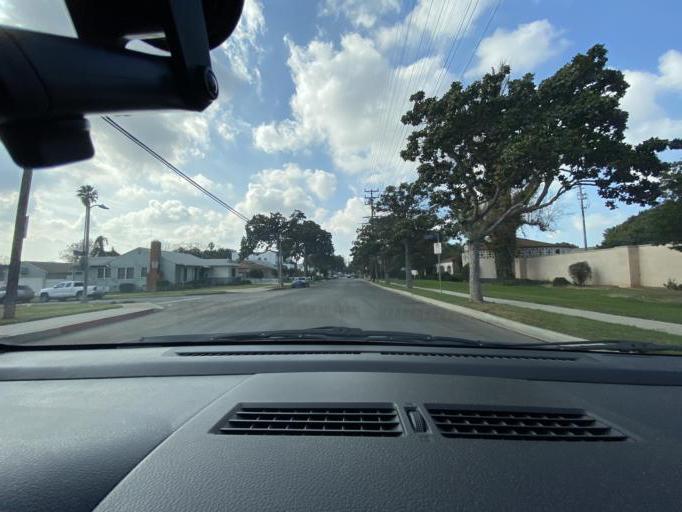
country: US
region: California
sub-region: Los Angeles County
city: Culver City
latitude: 34.0131
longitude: -118.4261
